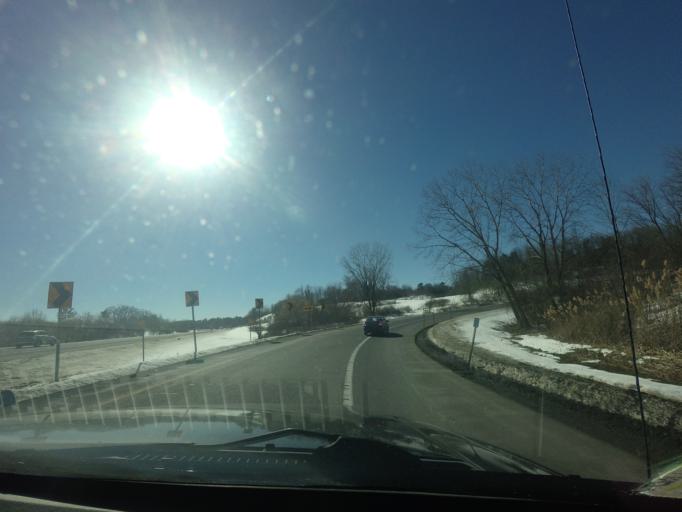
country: US
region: New York
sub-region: Rensselaer County
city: East Greenbush
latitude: 42.5581
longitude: -73.6807
